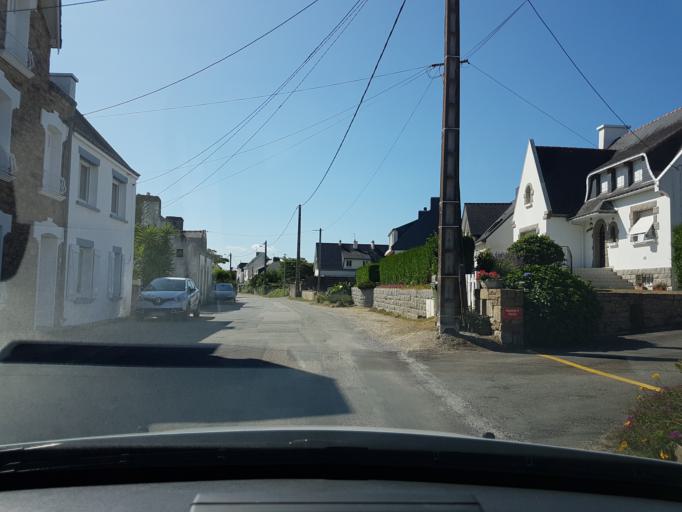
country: FR
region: Brittany
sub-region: Departement du Morbihan
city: Belz
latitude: 47.6815
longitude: -3.1852
